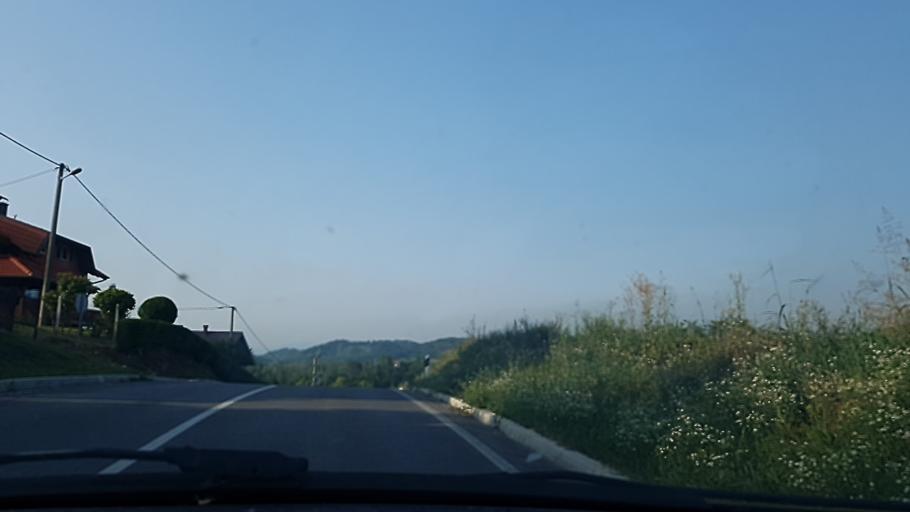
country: HR
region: Krapinsko-Zagorska
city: Zabok
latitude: 46.0175
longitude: 15.8540
